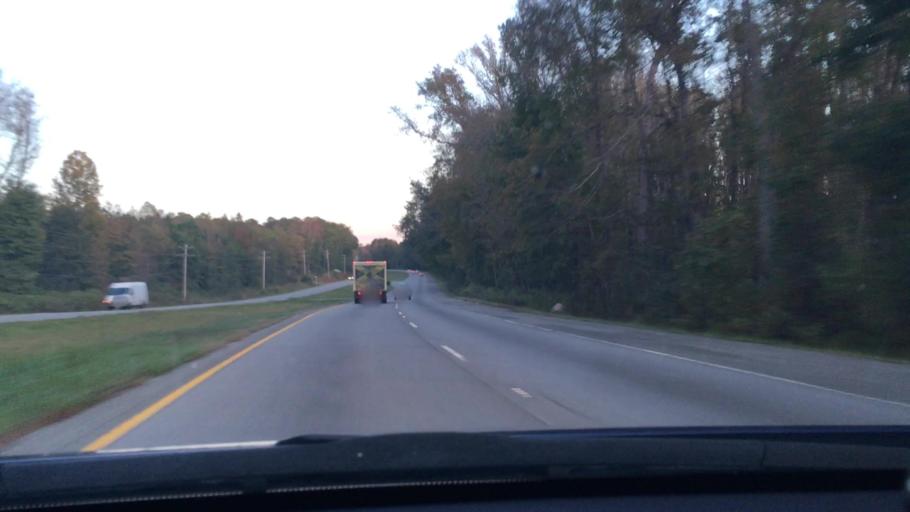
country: US
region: South Carolina
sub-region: Richland County
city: Gadsden
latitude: 33.9457
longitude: -80.7564
